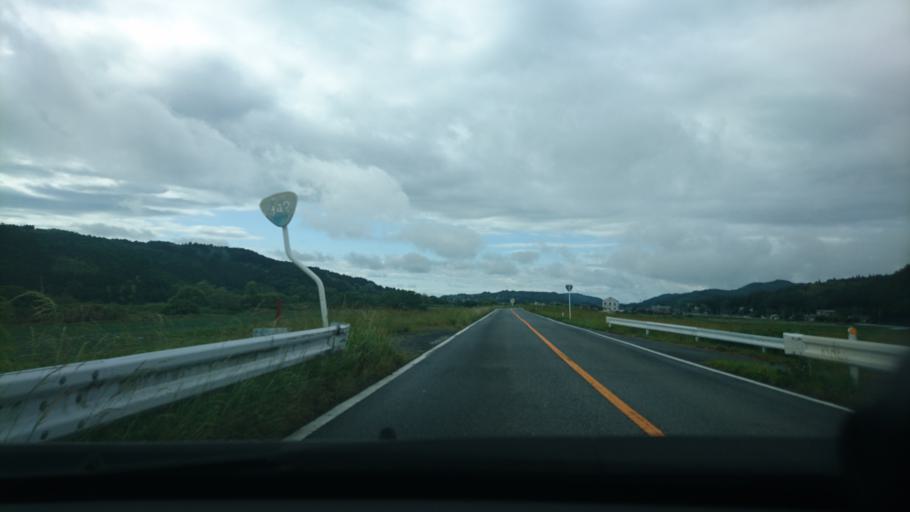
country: JP
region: Miyagi
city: Wakuya
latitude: 38.6354
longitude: 141.2893
